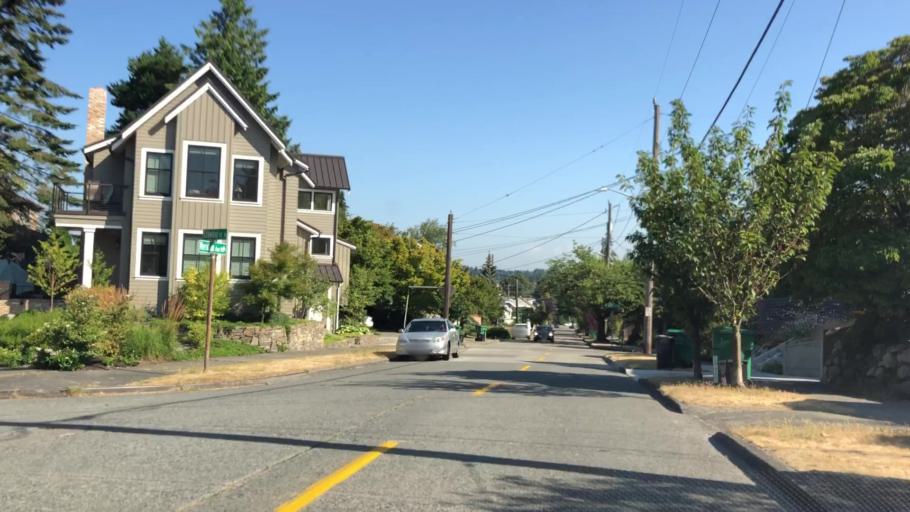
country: US
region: Washington
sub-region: King County
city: Seattle
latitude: 47.6718
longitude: -122.3336
